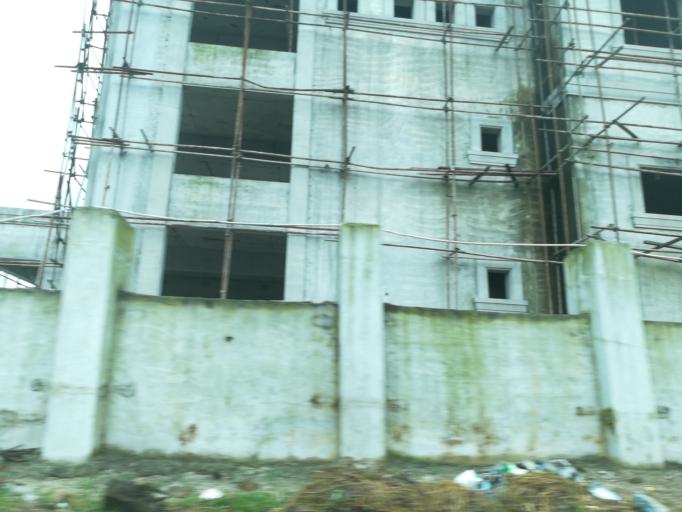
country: NG
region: Rivers
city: Port Harcourt
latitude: 4.8139
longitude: 6.9941
